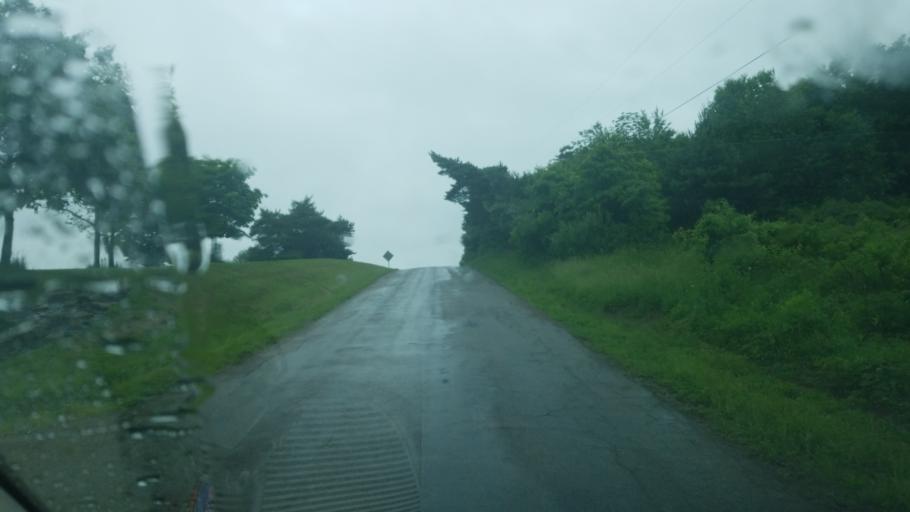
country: US
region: Ohio
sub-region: Sandusky County
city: Bellville
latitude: 40.6236
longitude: -82.4432
